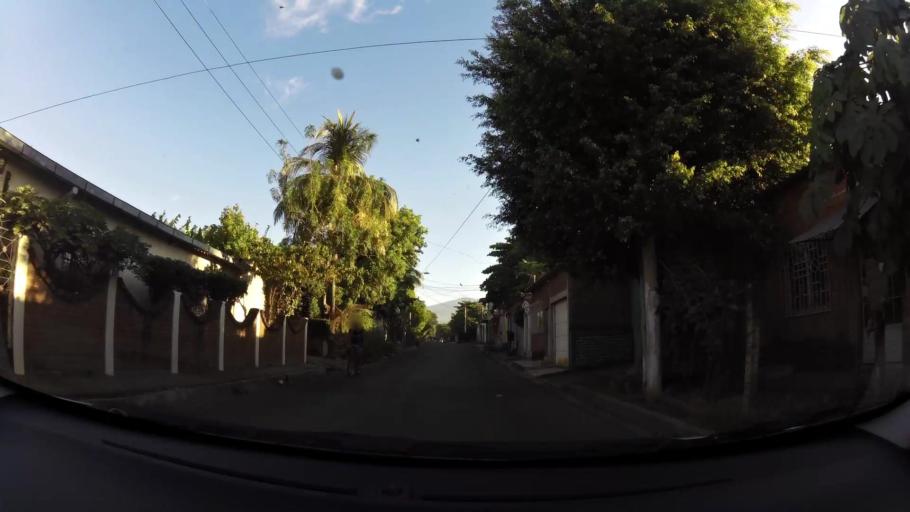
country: SV
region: Sonsonate
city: San Antonio del Monte
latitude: 13.7099
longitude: -89.7325
